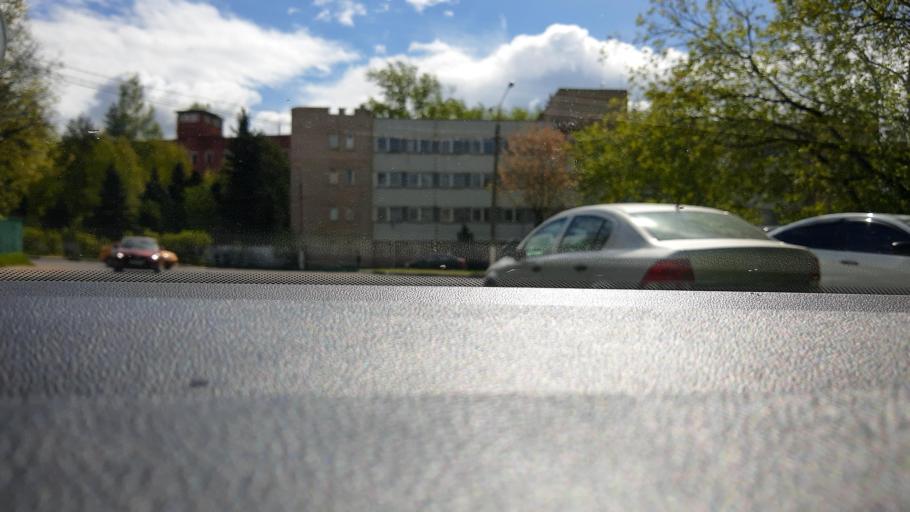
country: RU
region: Moskovskaya
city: Dmitrov
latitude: 56.3493
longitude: 37.5316
